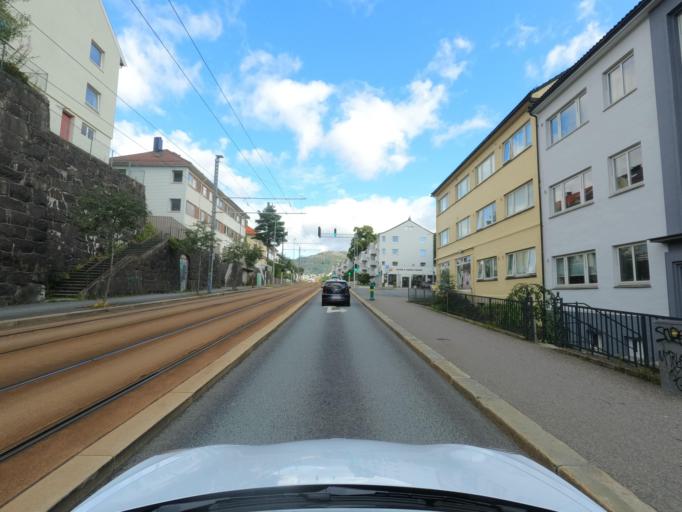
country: NO
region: Hordaland
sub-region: Bergen
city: Bergen
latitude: 60.3631
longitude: 5.3518
